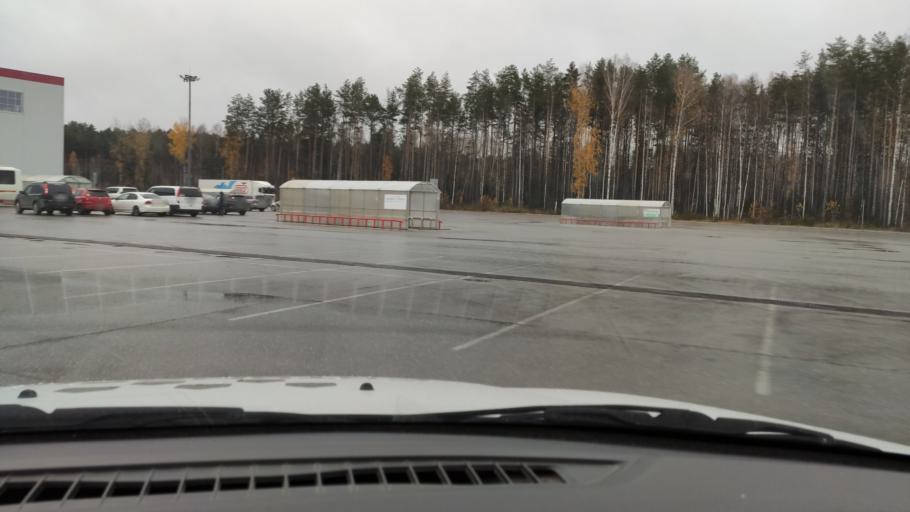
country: RU
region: Perm
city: Perm
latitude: 58.0392
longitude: 56.1940
